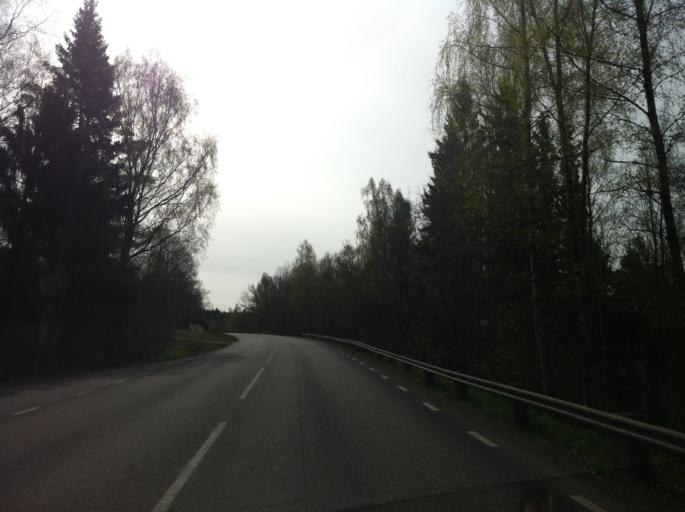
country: SE
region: Vaestra Goetaland
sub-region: Marks Kommun
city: Kinna
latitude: 57.4036
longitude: 12.7806
